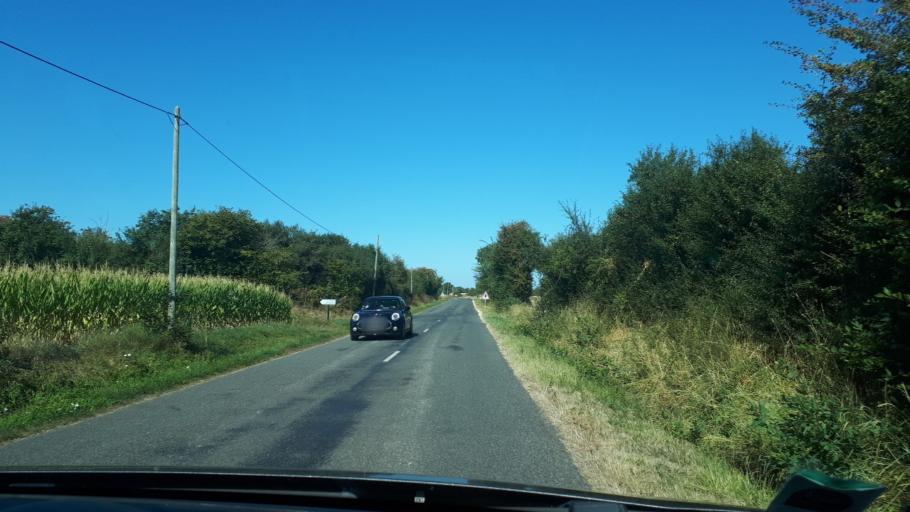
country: FR
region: Centre
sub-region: Departement du Loiret
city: Briare
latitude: 47.5908
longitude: 2.7240
